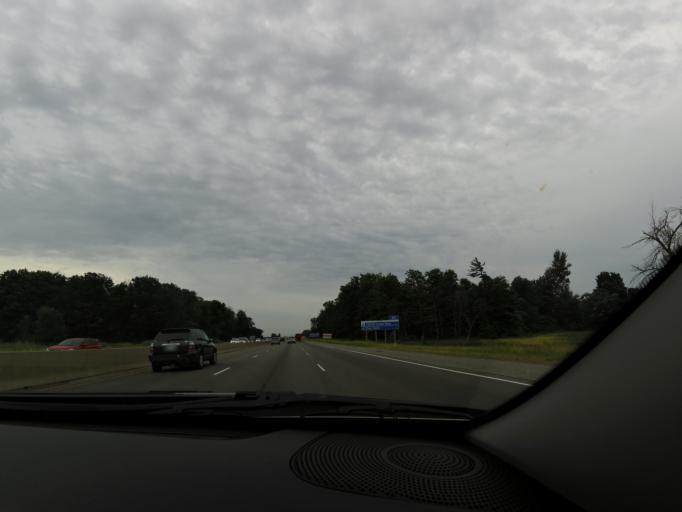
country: CA
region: Ontario
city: Vaughan
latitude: 43.9379
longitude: -79.5703
